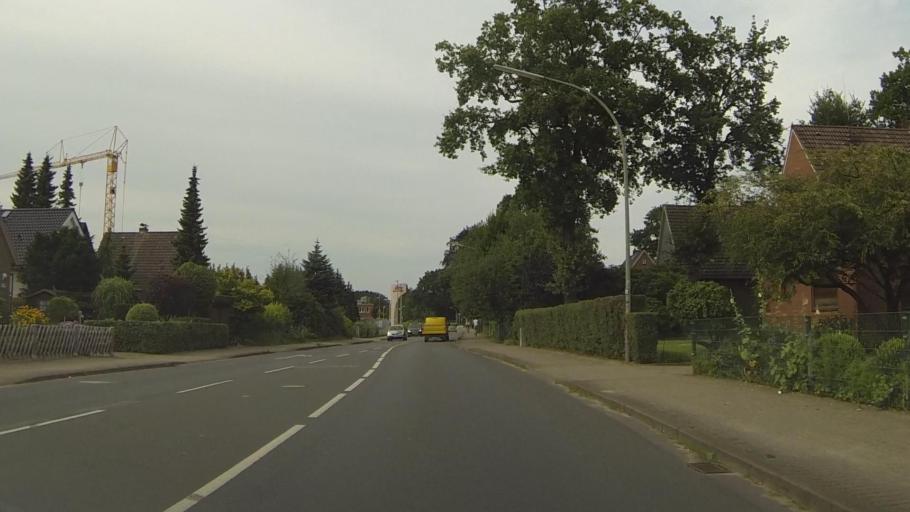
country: DE
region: Schleswig-Holstein
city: Ellerbek
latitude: 53.6319
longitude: 9.8727
